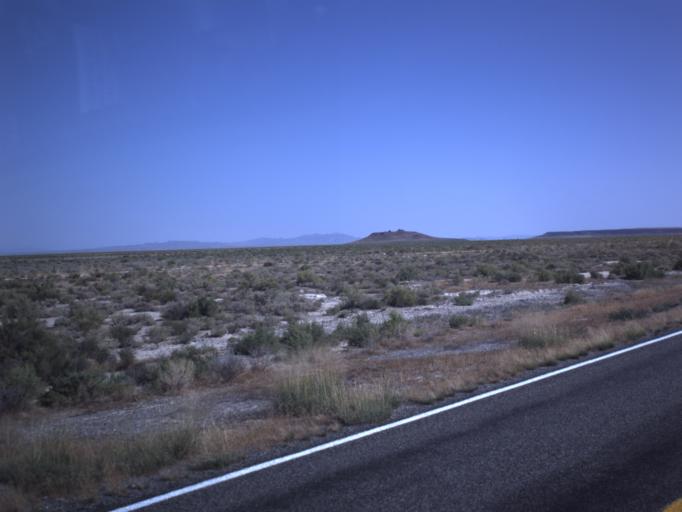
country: US
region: Utah
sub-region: Millard County
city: Delta
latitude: 39.0813
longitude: -112.7551
